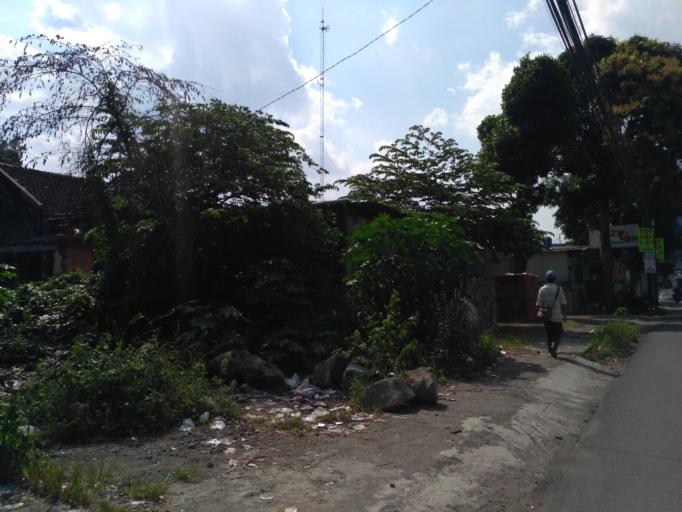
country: ID
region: Daerah Istimewa Yogyakarta
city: Depok
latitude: -7.7742
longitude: 110.4089
